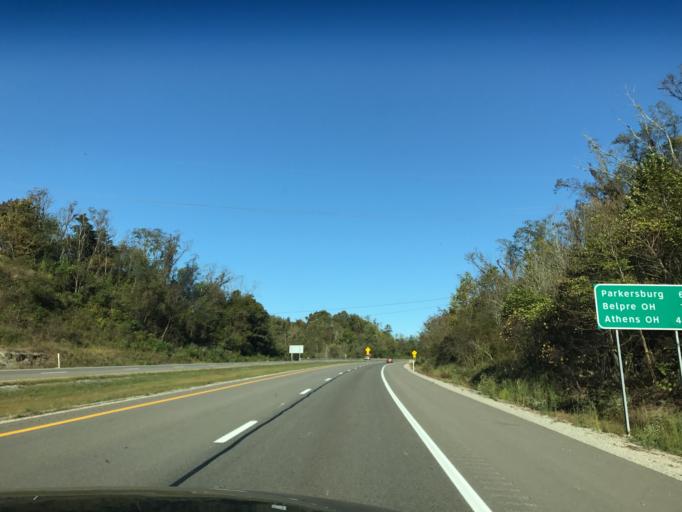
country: US
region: West Virginia
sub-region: Wood County
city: Mineral Wells
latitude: 39.2400
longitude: -81.4652
